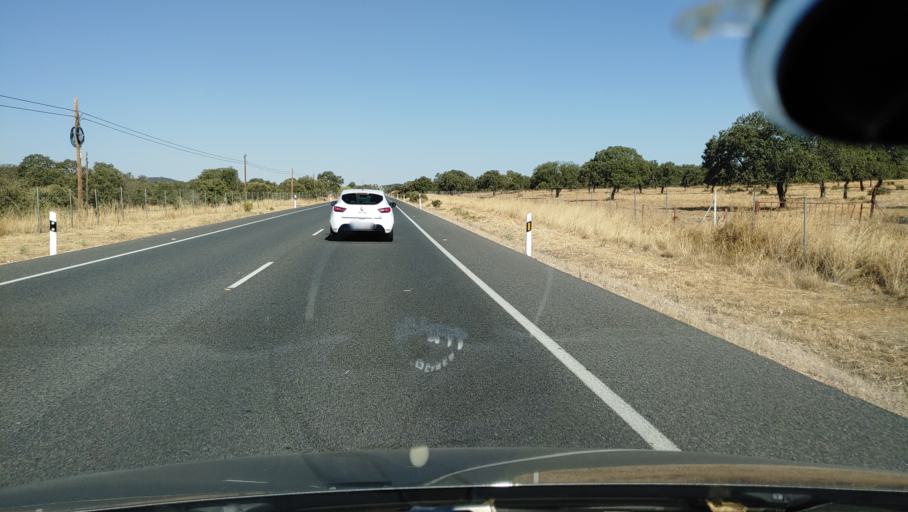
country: ES
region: Andalusia
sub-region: Province of Cordoba
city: Obejo
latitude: 38.0612
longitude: -4.8224
